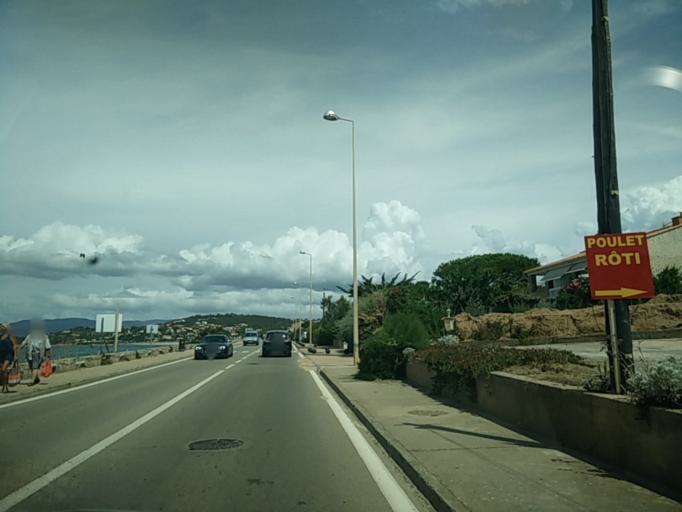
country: FR
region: Corsica
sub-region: Departement de la Corse-du-Sud
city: Pietrosella
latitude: 41.8566
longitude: 8.7911
